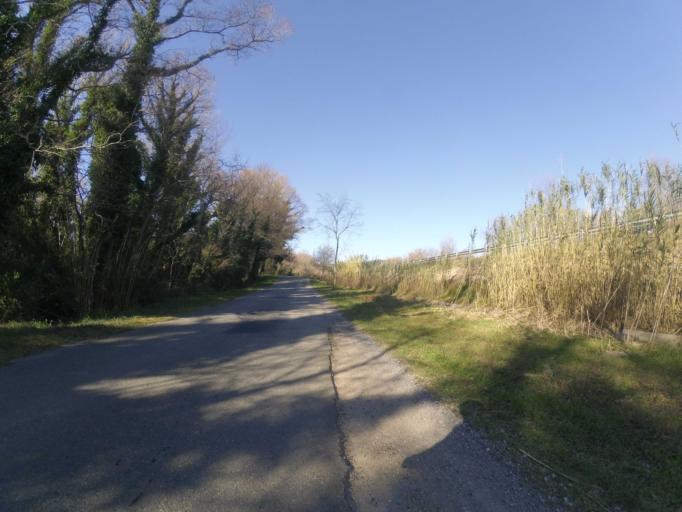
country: FR
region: Languedoc-Roussillon
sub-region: Departement des Pyrenees-Orientales
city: Millas
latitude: 42.6931
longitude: 2.6581
